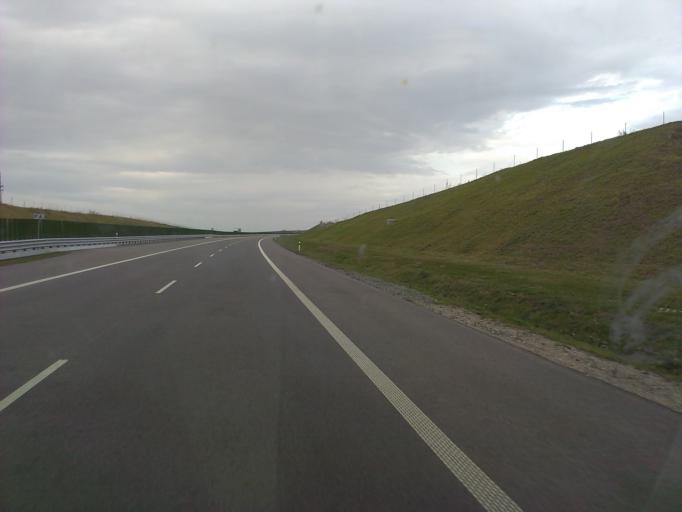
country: PL
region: Subcarpathian Voivodeship
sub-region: Powiat jaroslawski
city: Pawlosiow
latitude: 49.9466
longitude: 22.6664
